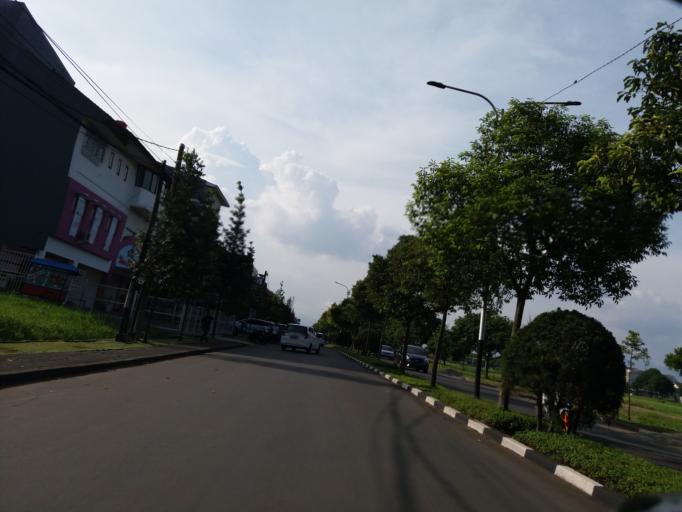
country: ID
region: West Java
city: Bandung
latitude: -6.9585
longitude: 107.6265
